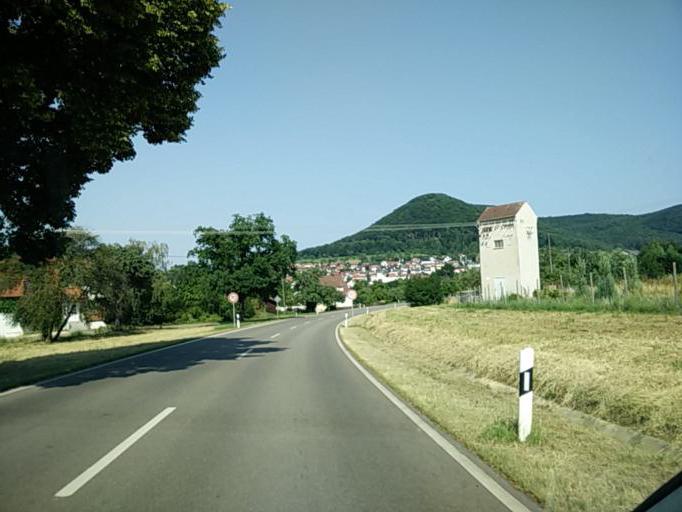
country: DE
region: Baden-Wuerttemberg
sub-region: Tuebingen Region
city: Gomaringen
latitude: 48.4366
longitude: 9.1376
